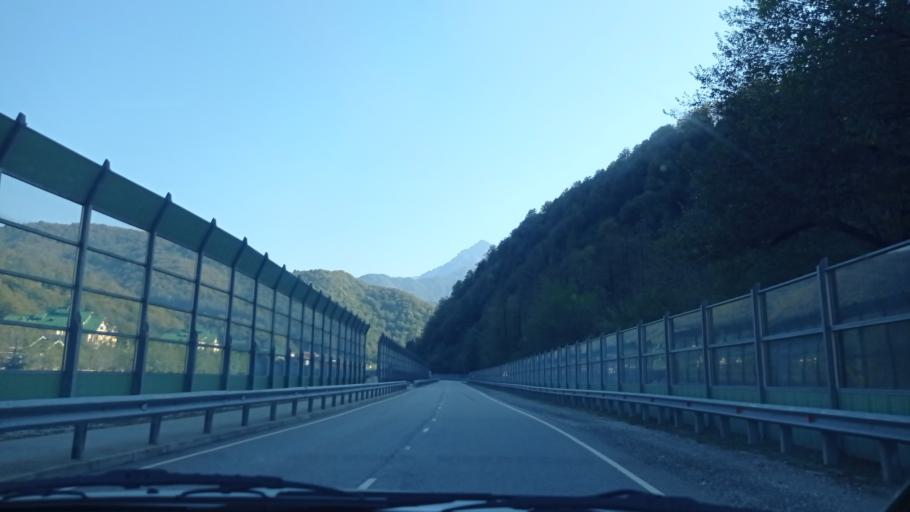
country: RU
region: Krasnodarskiy
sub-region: Sochi City
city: Krasnaya Polyana
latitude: 43.6937
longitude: 40.2694
